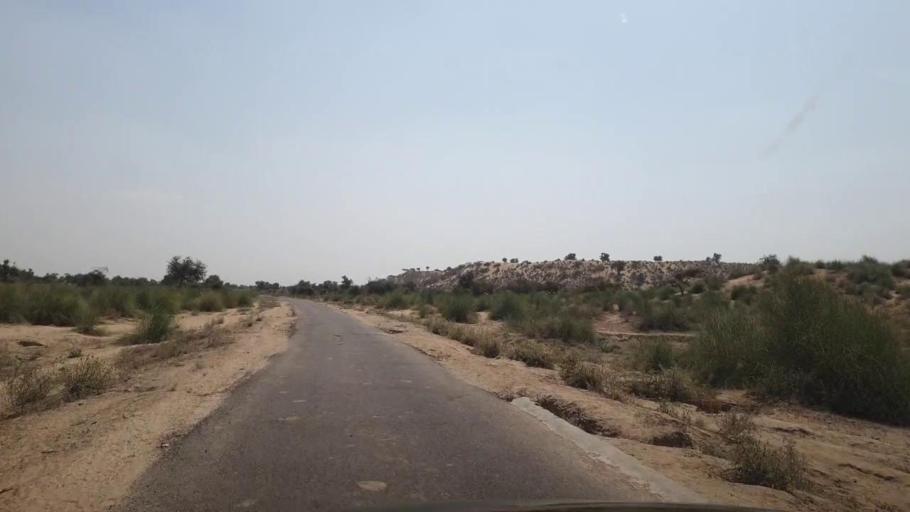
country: PK
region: Sindh
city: Islamkot
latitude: 25.1056
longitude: 70.7227
